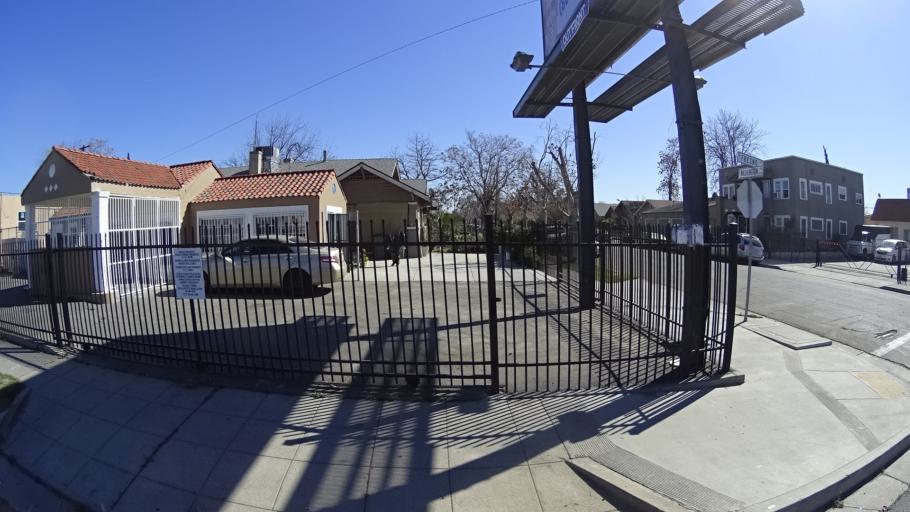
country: US
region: California
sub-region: Fresno County
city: Fresno
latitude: 36.7479
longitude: -119.7815
